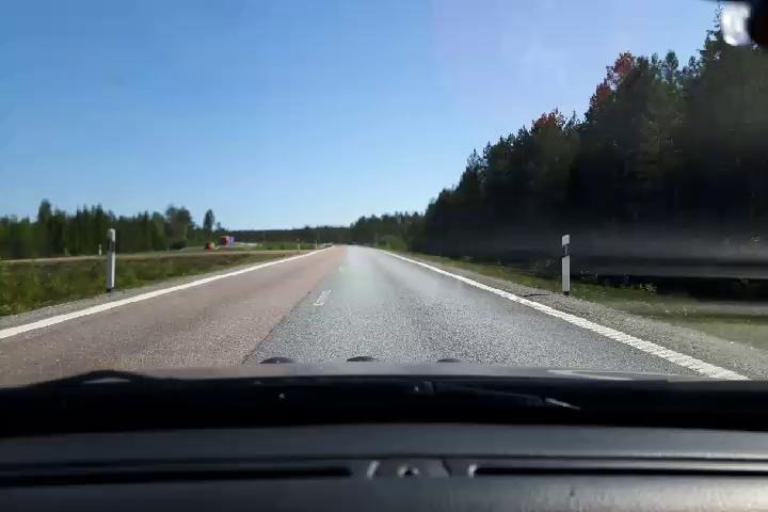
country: SE
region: Gaevleborg
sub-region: Soderhamns Kommun
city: Soderhamn
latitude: 61.3825
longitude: 16.9924
